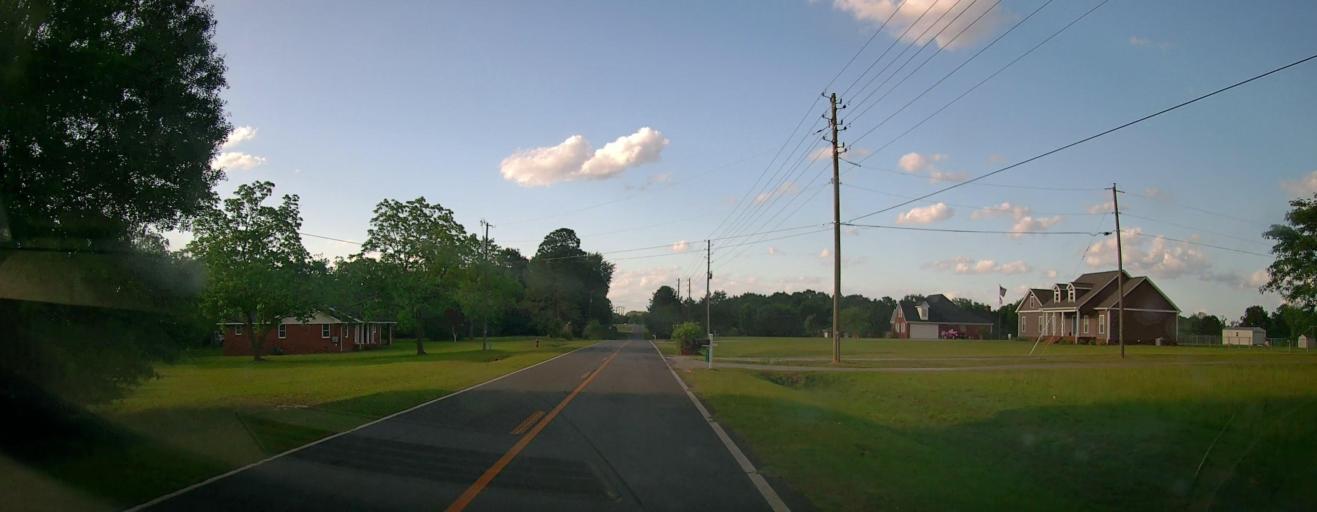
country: US
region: Georgia
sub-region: Peach County
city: Byron
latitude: 32.6331
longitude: -83.7671
